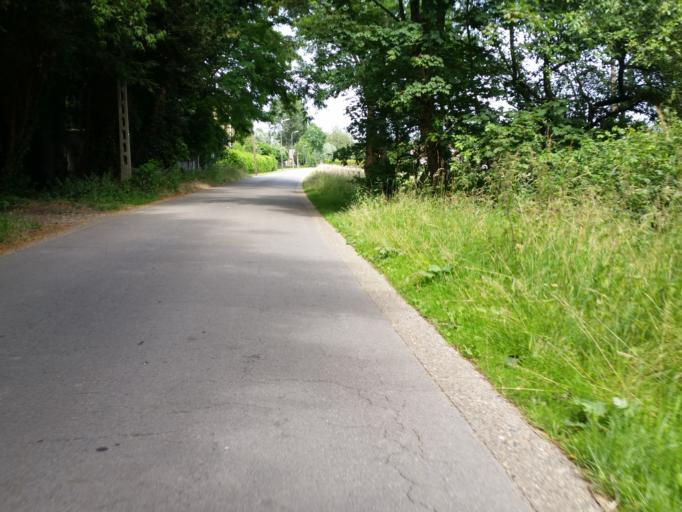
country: BE
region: Flanders
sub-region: Provincie Antwerpen
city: Rumst
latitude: 51.0686
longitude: 4.4111
